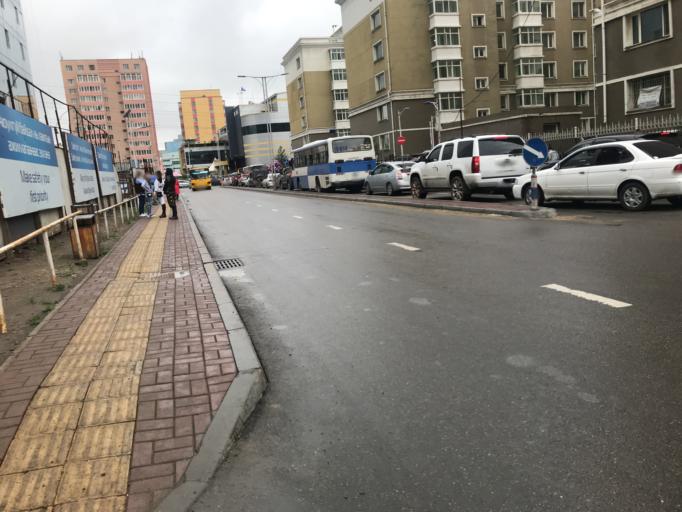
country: MN
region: Ulaanbaatar
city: Ulaanbaatar
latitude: 47.9043
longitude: 106.9298
